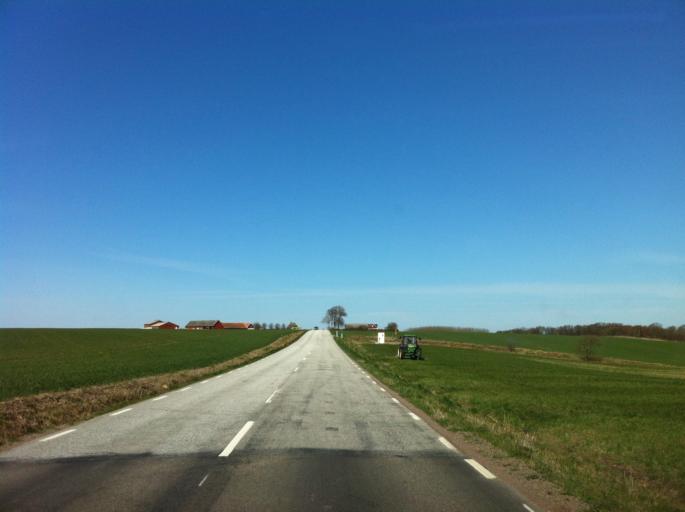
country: SE
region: Skane
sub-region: Helsingborg
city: Glumslov
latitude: 55.9693
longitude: 12.8268
